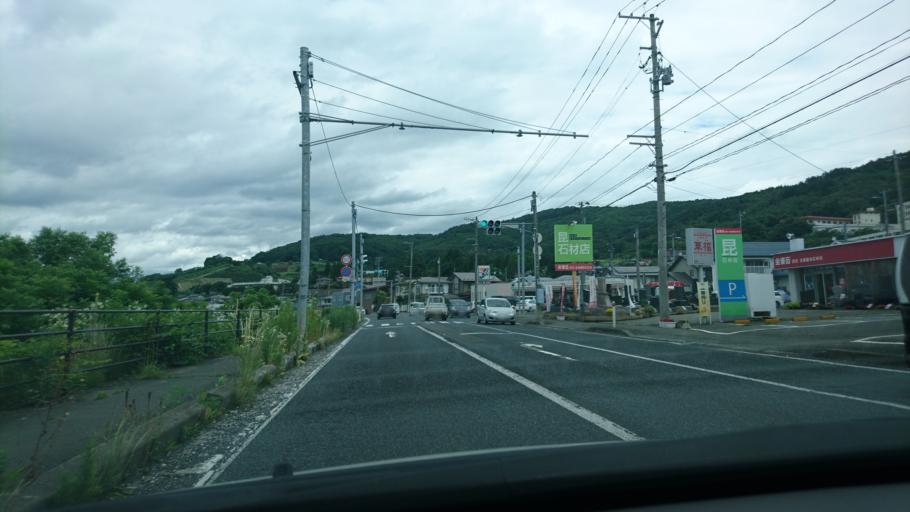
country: JP
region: Iwate
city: Morioka-shi
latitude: 39.6559
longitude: 141.1821
